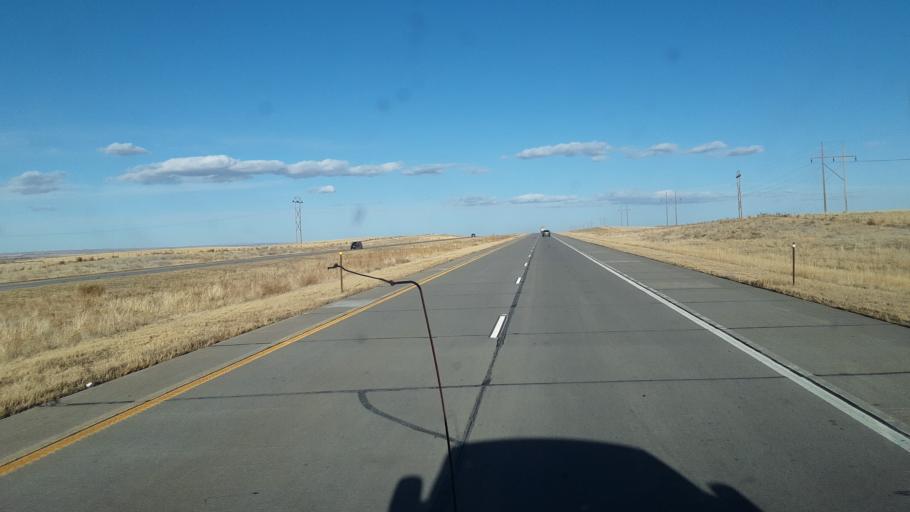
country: US
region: Colorado
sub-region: Logan County
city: Sterling
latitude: 40.7322
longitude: -103.0147
